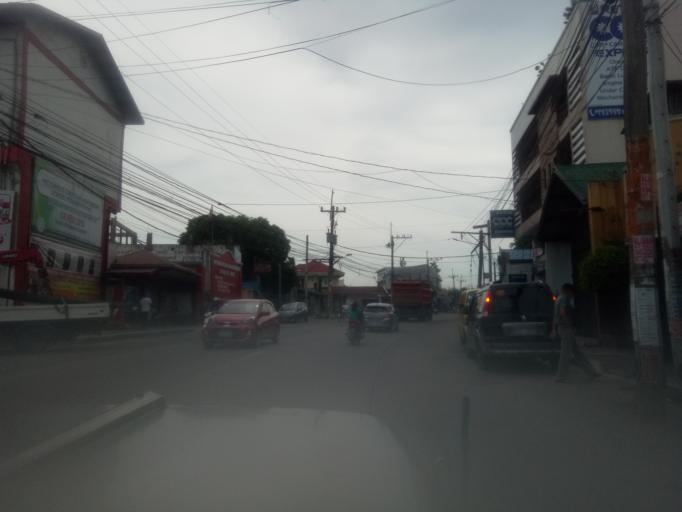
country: PH
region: Calabarzon
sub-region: Province of Cavite
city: Bulihan
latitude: 14.2903
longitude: 121.0040
